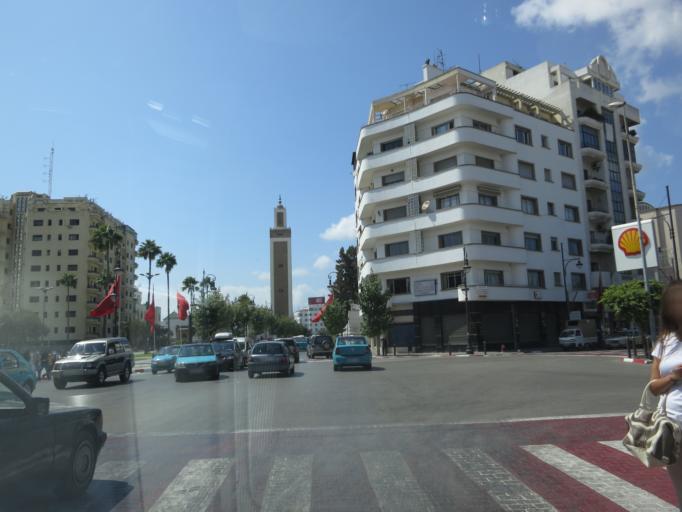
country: MA
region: Tanger-Tetouan
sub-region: Tanger-Assilah
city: Tangier
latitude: 35.7810
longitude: -5.8168
